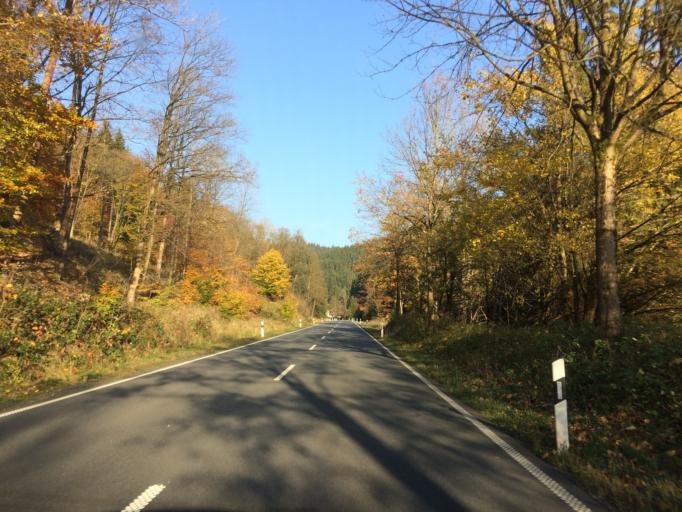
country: DE
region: Lower Saxony
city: Wieda
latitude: 51.6763
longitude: 10.5626
